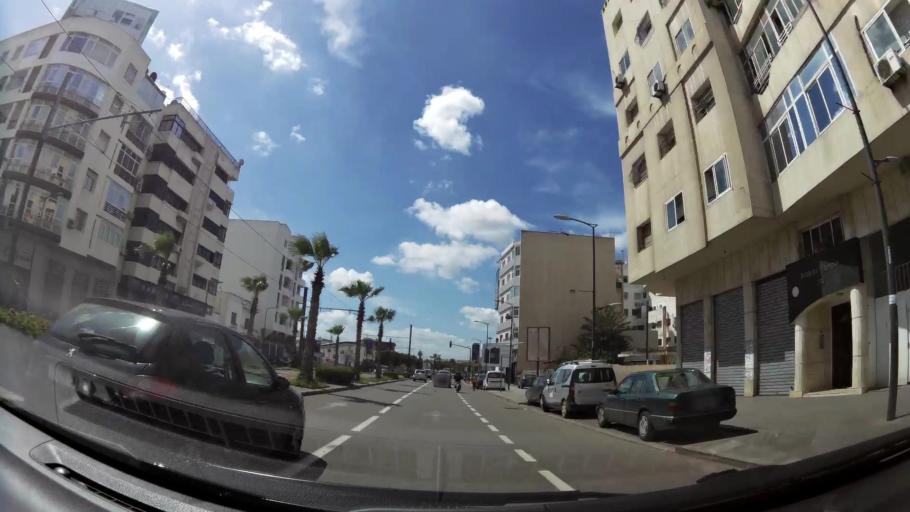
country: MA
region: Grand Casablanca
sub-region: Casablanca
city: Casablanca
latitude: 33.5672
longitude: -7.6263
